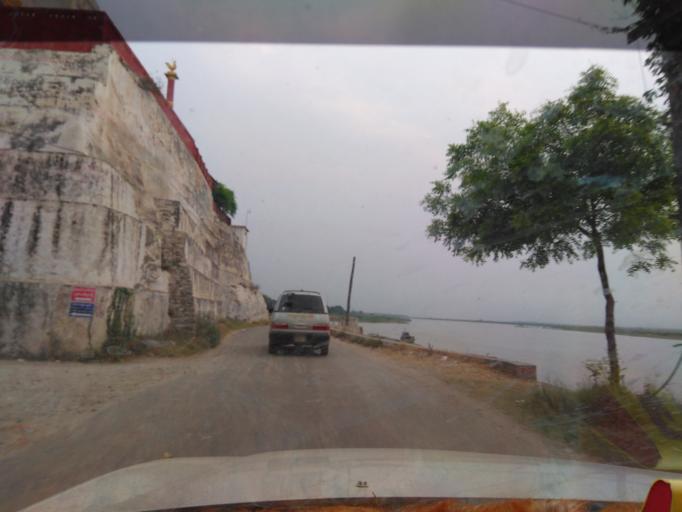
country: MM
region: Sagain
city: Sagaing
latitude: 21.9067
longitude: 96.0014
